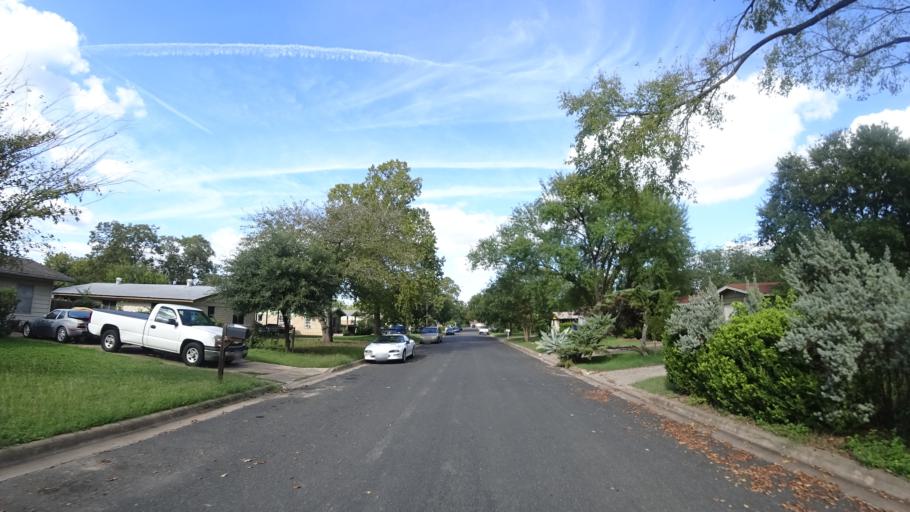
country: US
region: Texas
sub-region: Travis County
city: Rollingwood
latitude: 30.2079
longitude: -97.7903
